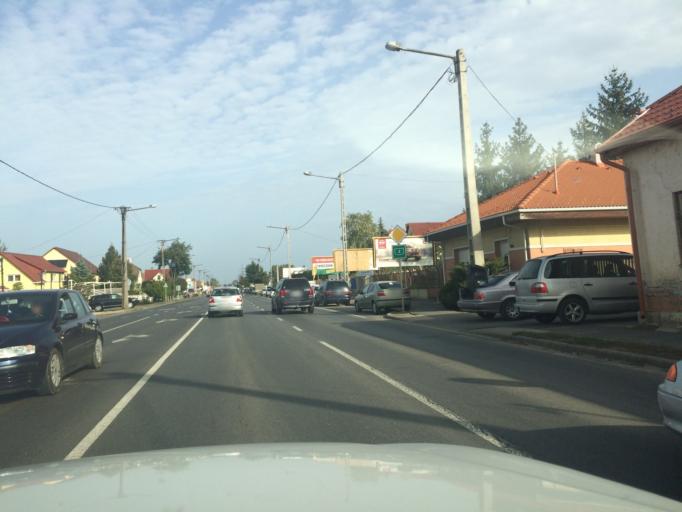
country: HU
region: Szabolcs-Szatmar-Bereg
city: Nyiregyhaza
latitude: 47.9257
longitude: 21.7187
